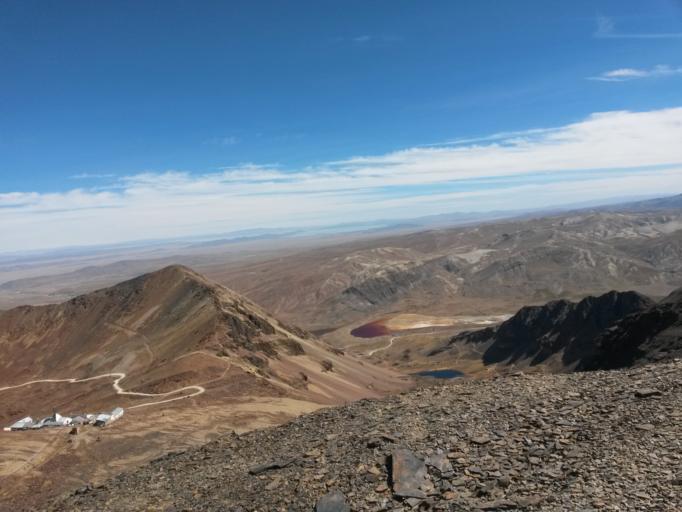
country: BO
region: La Paz
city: La Paz
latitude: -16.3497
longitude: -68.1276
